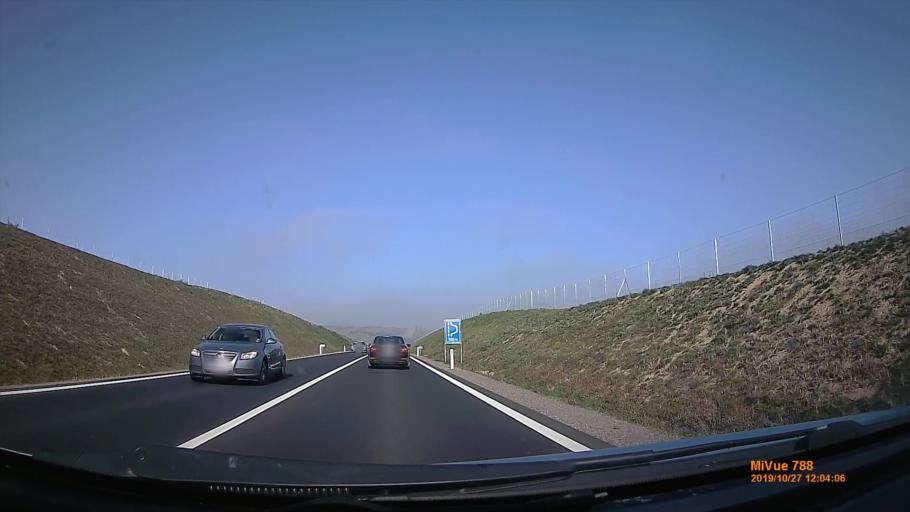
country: AT
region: Lower Austria
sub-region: Politischer Bezirk Mistelbach
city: Drasenhofen
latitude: 48.7497
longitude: 16.6356
